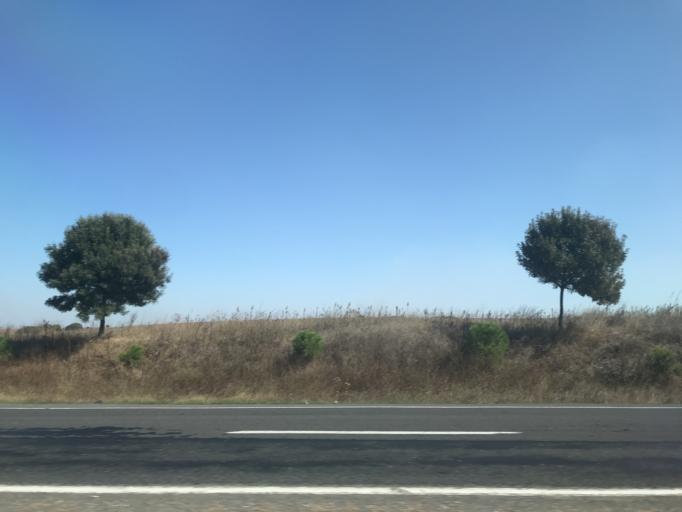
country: TR
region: Tekirdag
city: Muratli
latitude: 41.1130
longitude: 27.4915
